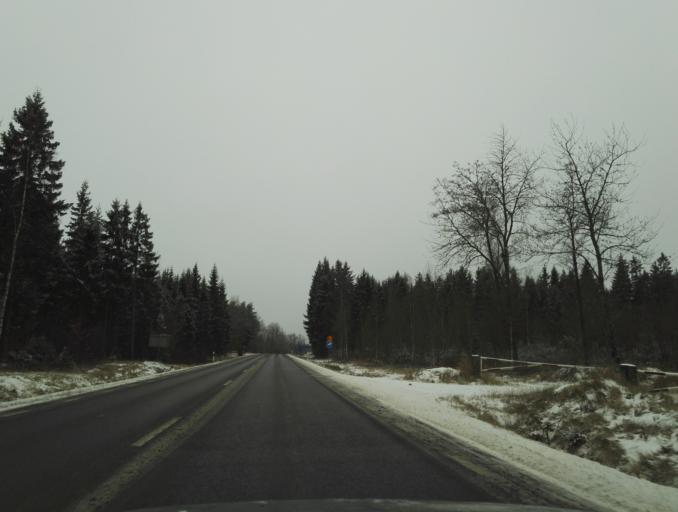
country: SE
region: Kronoberg
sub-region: Vaxjo Kommun
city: Gemla
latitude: 56.8202
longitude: 14.6879
